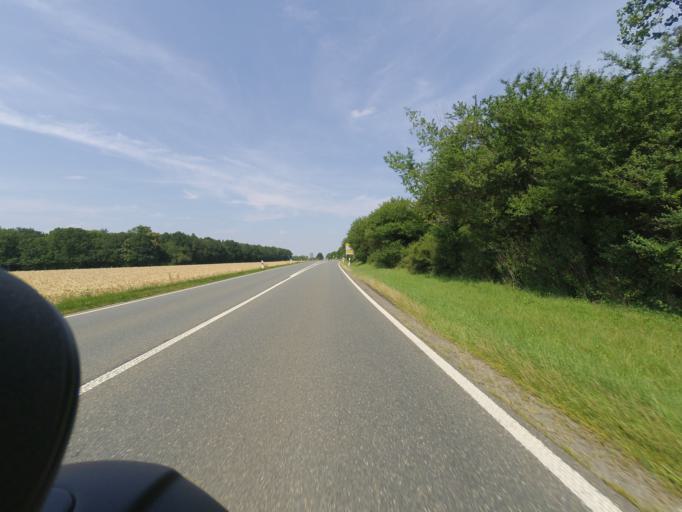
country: DE
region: Thuringia
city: Schwaara
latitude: 50.9558
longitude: 12.1224
